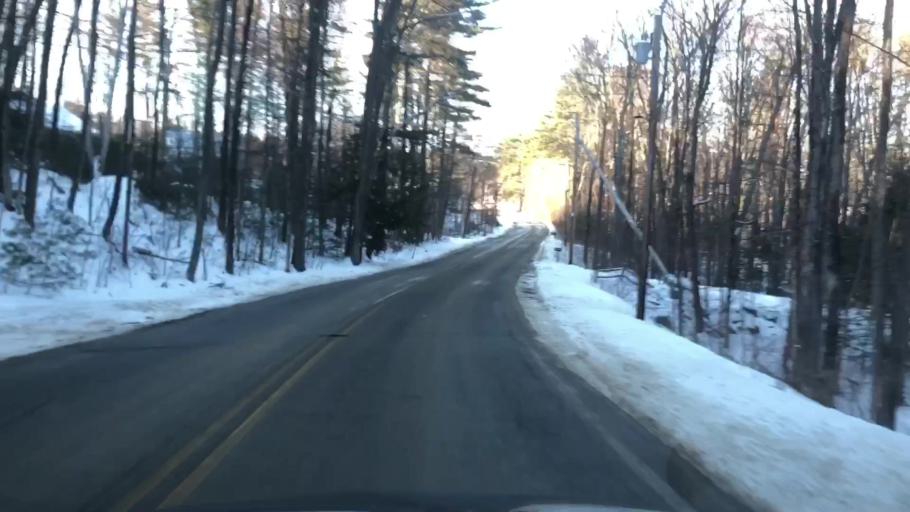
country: US
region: New Hampshire
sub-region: Hillsborough County
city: Milford
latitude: 42.8079
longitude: -71.6680
